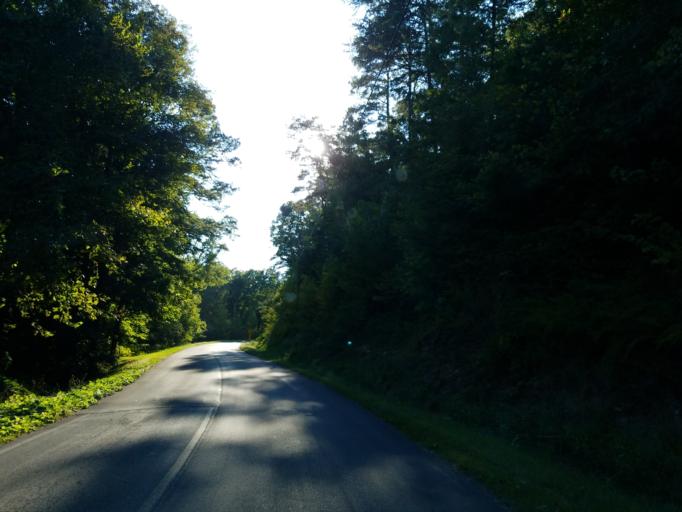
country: US
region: Georgia
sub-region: Murray County
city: Chatsworth
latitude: 34.9454
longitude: -84.7223
